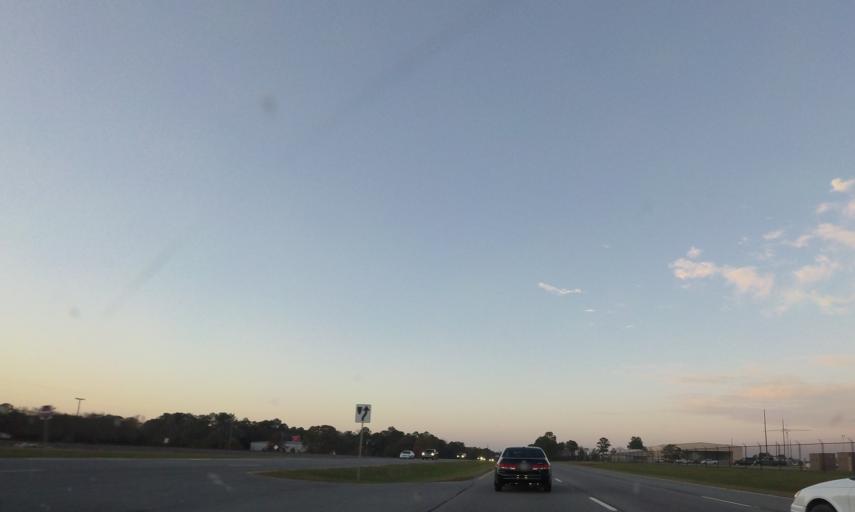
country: US
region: Georgia
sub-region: Houston County
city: Warner Robins
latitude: 32.6344
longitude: -83.6043
